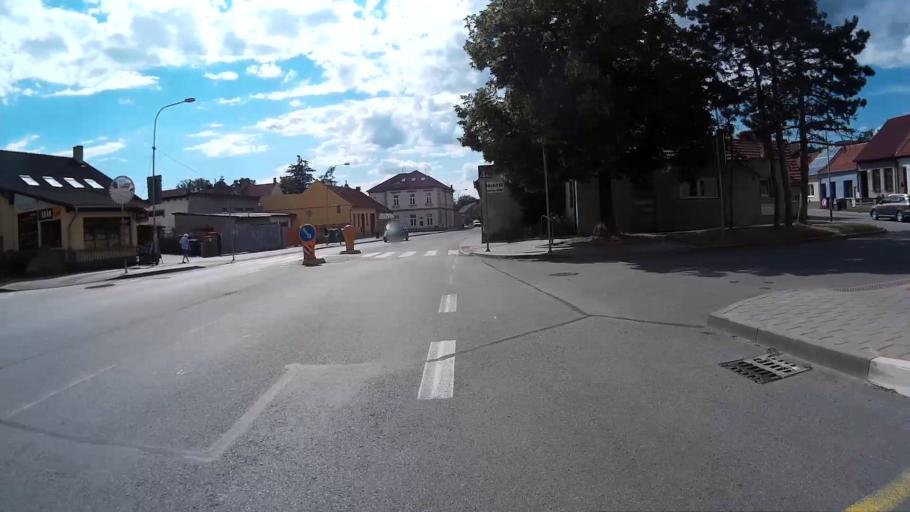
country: CZ
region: South Moravian
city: Ostopovice
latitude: 49.1644
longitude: 16.5655
